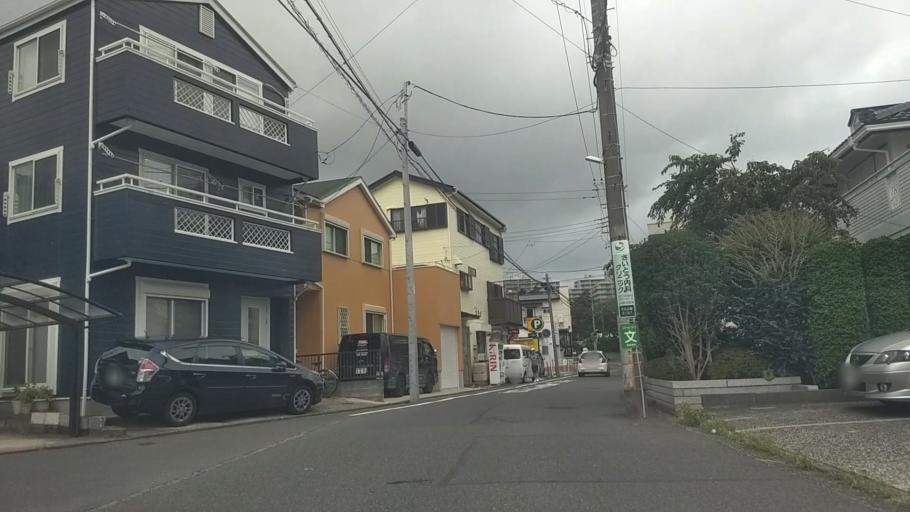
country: JP
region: Kanagawa
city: Yokosuka
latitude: 35.2703
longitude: 139.6614
